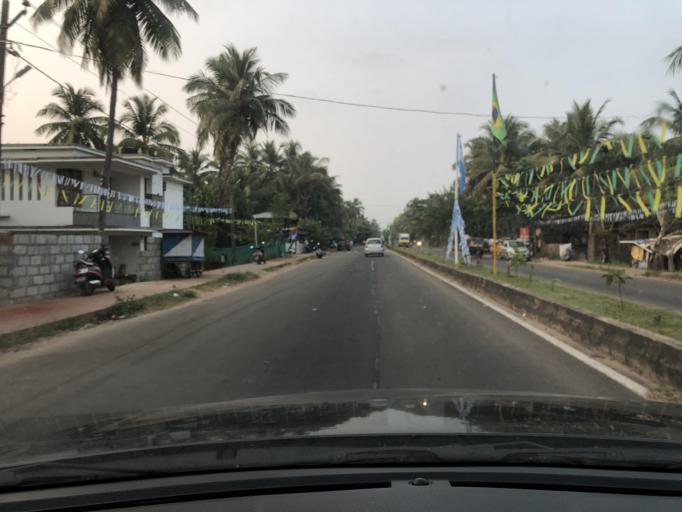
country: IN
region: Kerala
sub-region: Kozhikode
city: Kozhikode
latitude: 11.2960
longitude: 75.7567
